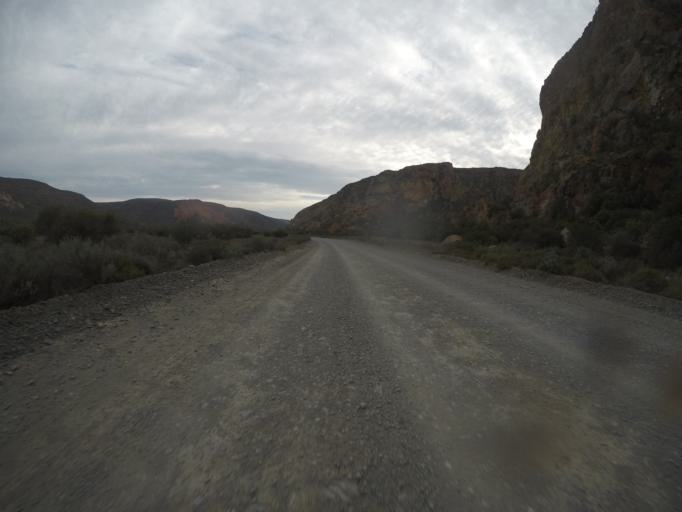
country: ZA
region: Eastern Cape
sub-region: Cacadu District Municipality
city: Willowmore
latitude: -33.5207
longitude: 23.6633
